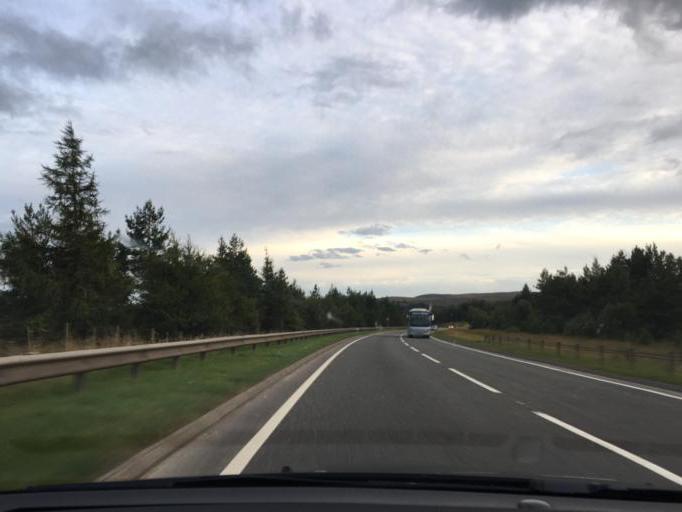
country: GB
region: Scotland
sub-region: Highland
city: Aviemore
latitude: 57.3552
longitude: -4.0047
